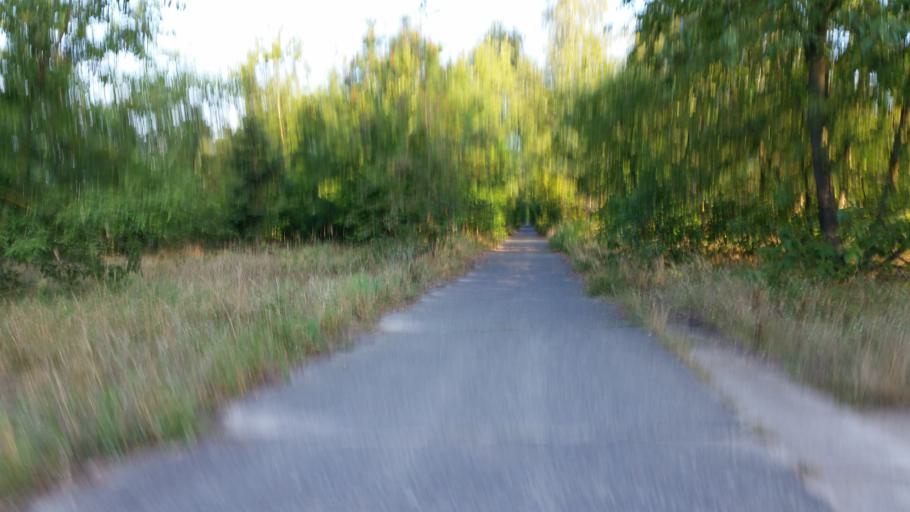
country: DE
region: Berlin
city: Marienfelde
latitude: 52.4059
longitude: 13.3451
